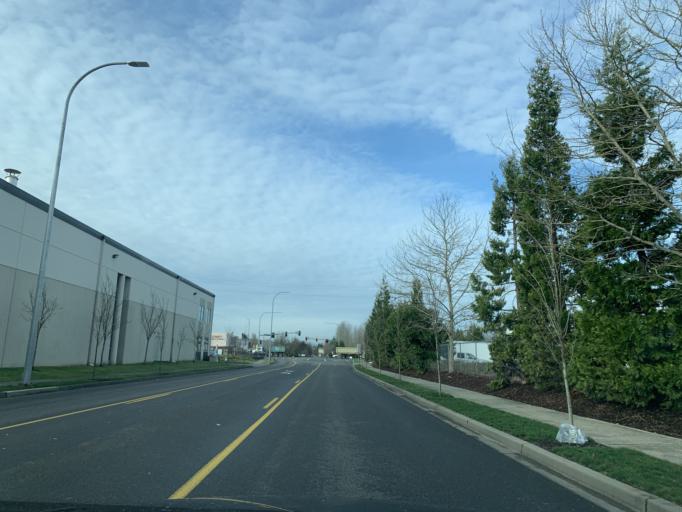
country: US
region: Washington
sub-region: Pierce County
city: Fife
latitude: 47.2336
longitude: -122.3341
